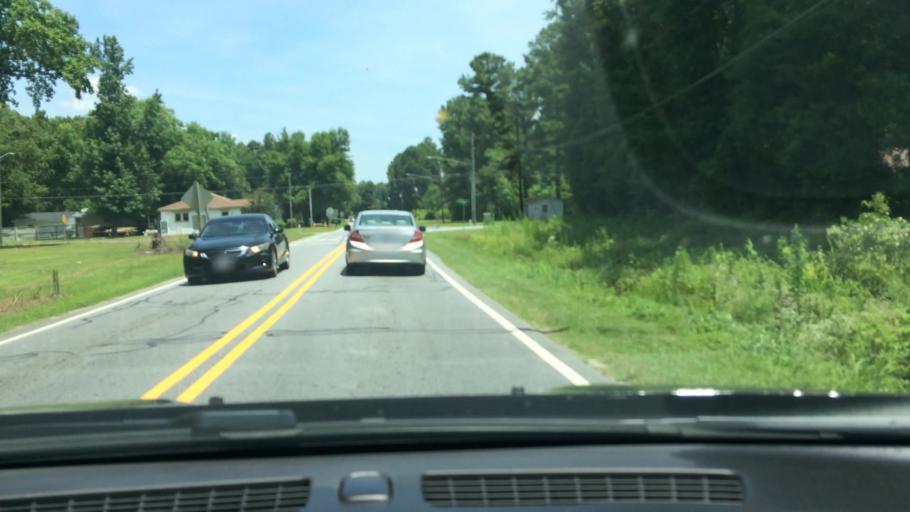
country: US
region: North Carolina
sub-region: Beaufort County
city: Washington
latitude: 35.5654
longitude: -77.1881
